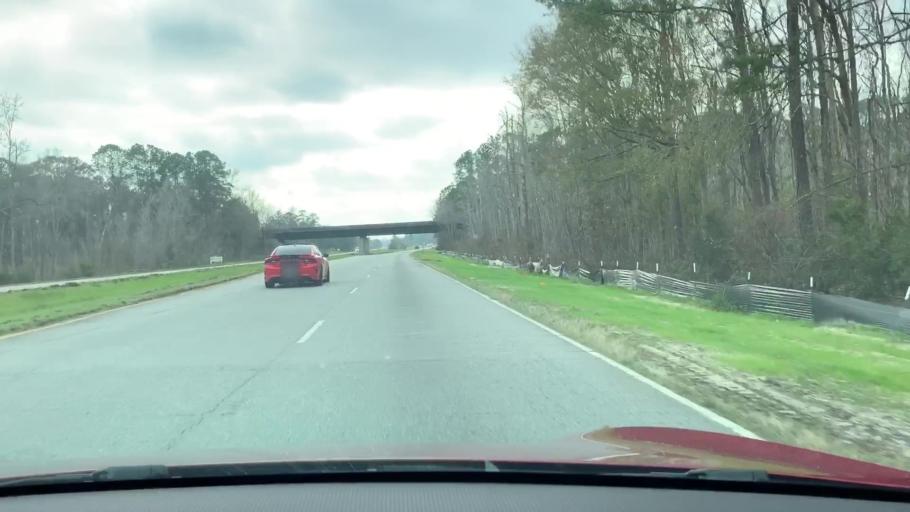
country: US
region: South Carolina
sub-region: Jasper County
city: Hardeeville
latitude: 32.2046
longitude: -81.0730
